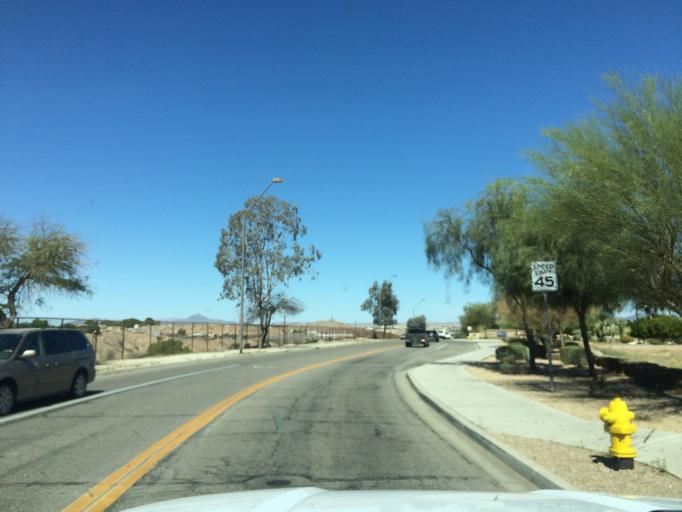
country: US
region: Arizona
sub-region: Yuma County
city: Yuma
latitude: 32.6995
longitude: -114.6115
